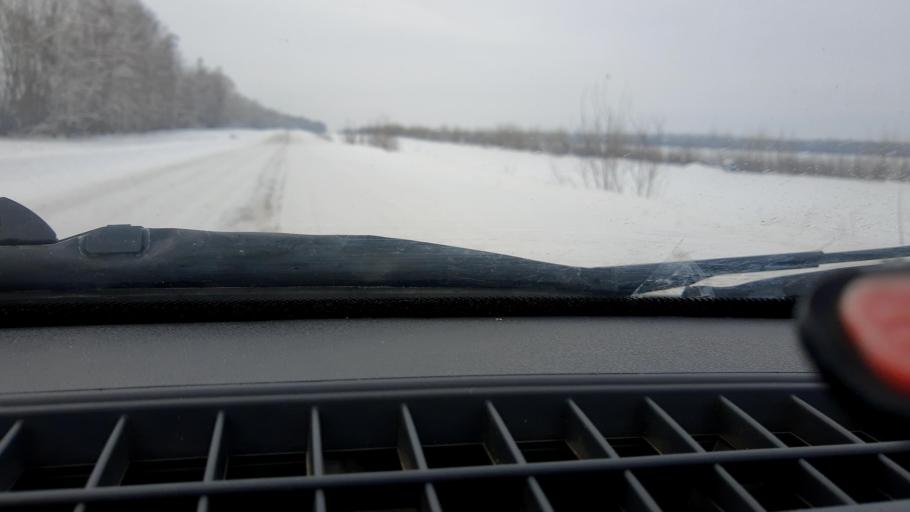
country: RU
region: Bashkortostan
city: Davlekanovo
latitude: 54.5620
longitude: 54.9894
